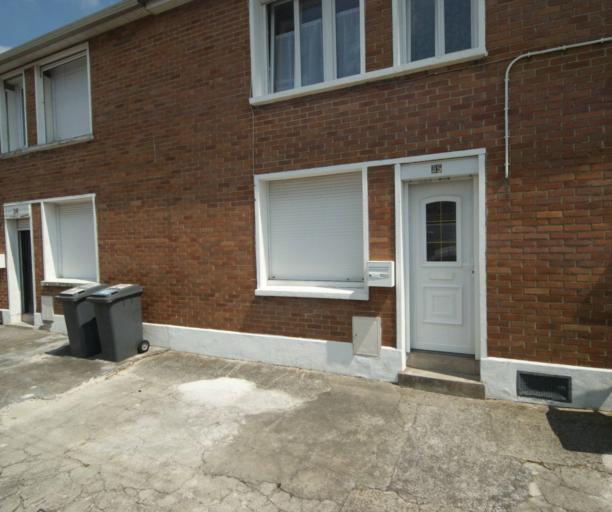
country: FR
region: Nord-Pas-de-Calais
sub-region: Departement du Nord
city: Armentieres
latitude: 50.6956
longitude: 2.8852
